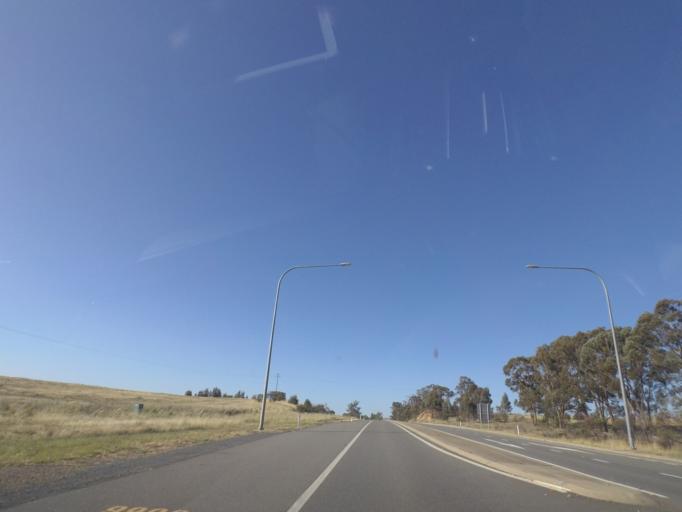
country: AU
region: New South Wales
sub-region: Wagga Wagga
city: Forest Hill
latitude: -35.2674
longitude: 147.7458
